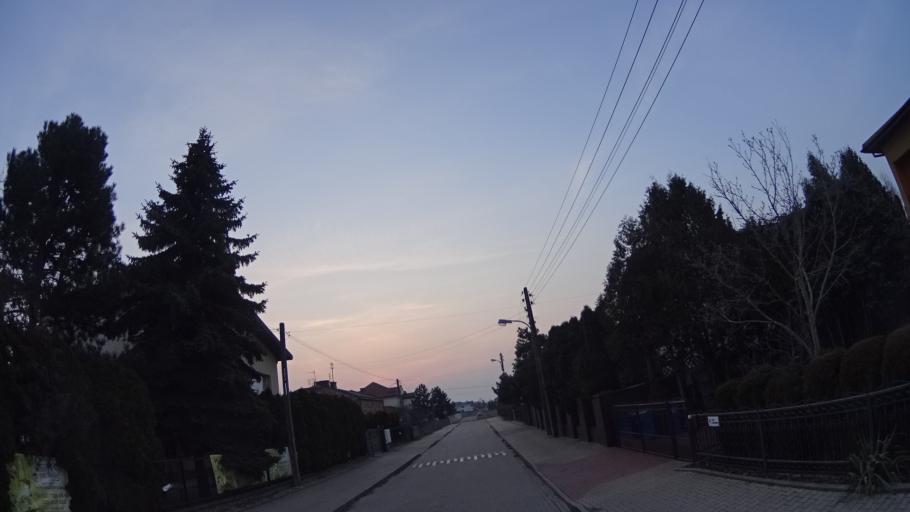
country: PL
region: Masovian Voivodeship
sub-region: Powiat warszawski zachodni
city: Babice
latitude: 52.2452
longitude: 20.8747
